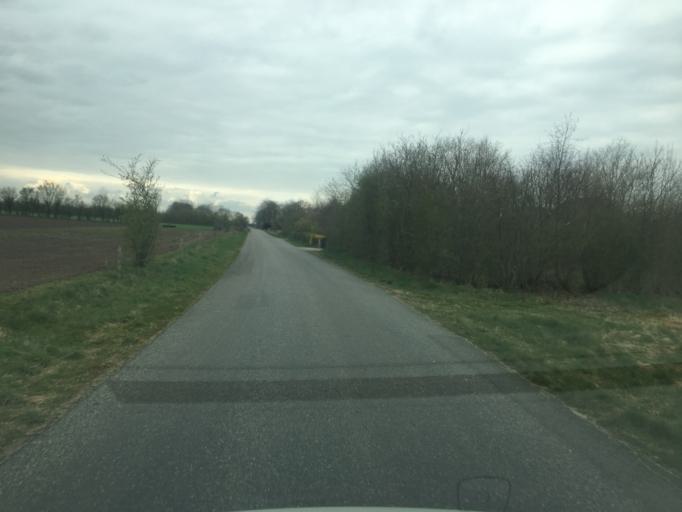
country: DK
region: South Denmark
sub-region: Tonder Kommune
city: Toftlund
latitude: 55.0484
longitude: 9.1247
